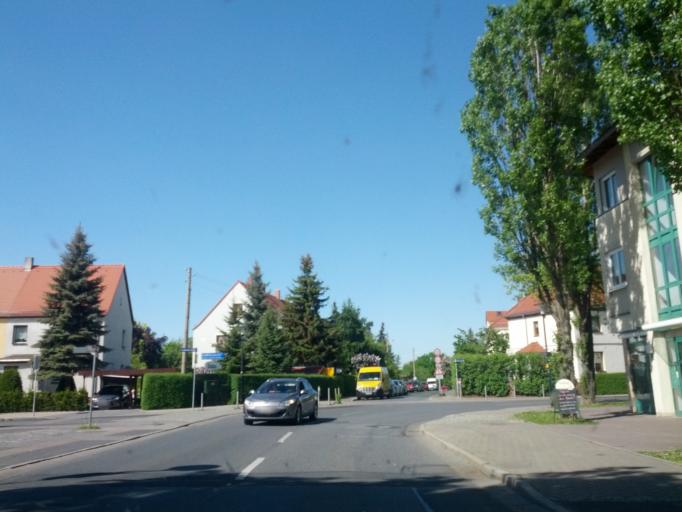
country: DE
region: Saxony
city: Bannewitz
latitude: 51.0065
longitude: 13.7659
